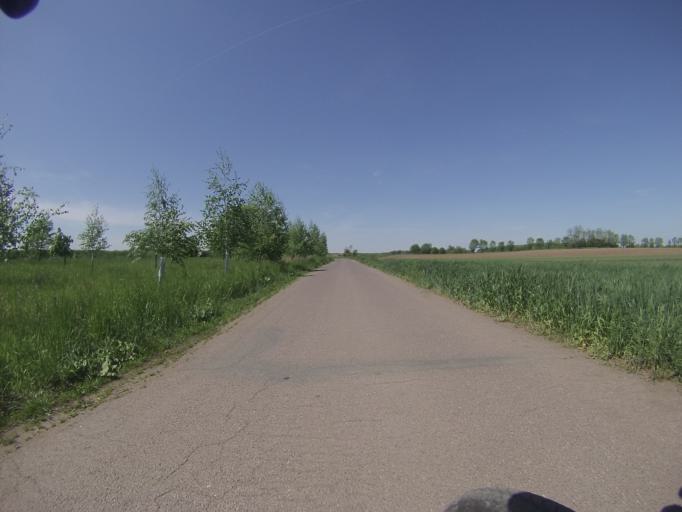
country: CZ
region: South Moravian
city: Novosedly
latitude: 48.8087
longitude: 16.4860
